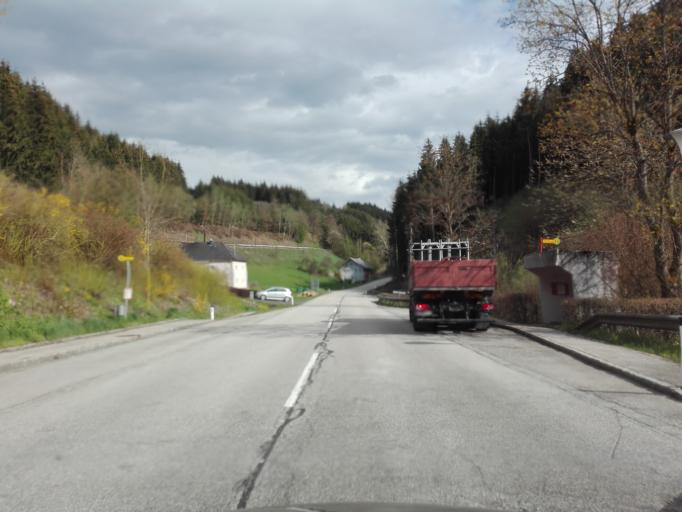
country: AT
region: Upper Austria
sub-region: Politischer Bezirk Rohrbach
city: Kleinzell im Muehlkreis
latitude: 48.4797
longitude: 14.0029
